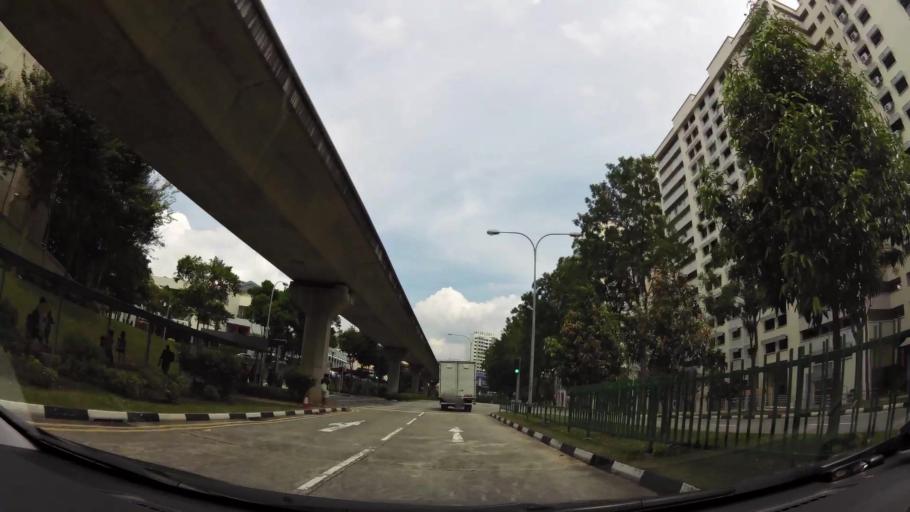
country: MY
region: Johor
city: Johor Bahru
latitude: 1.3873
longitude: 103.7651
